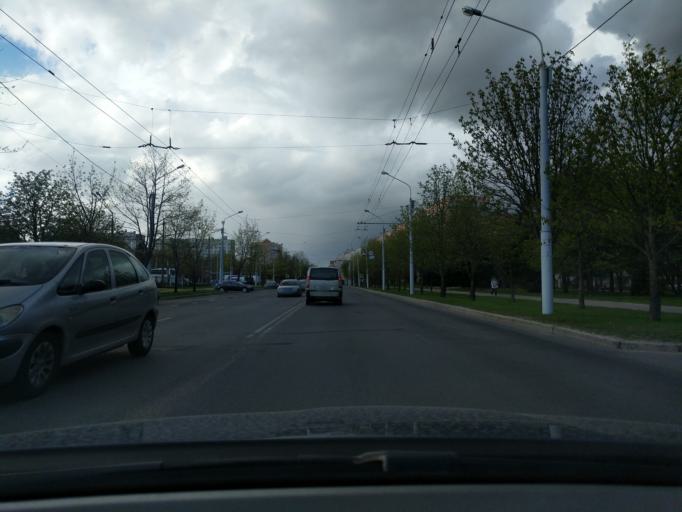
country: BY
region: Minsk
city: Novoye Medvezhino
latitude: 53.8991
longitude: 27.4815
